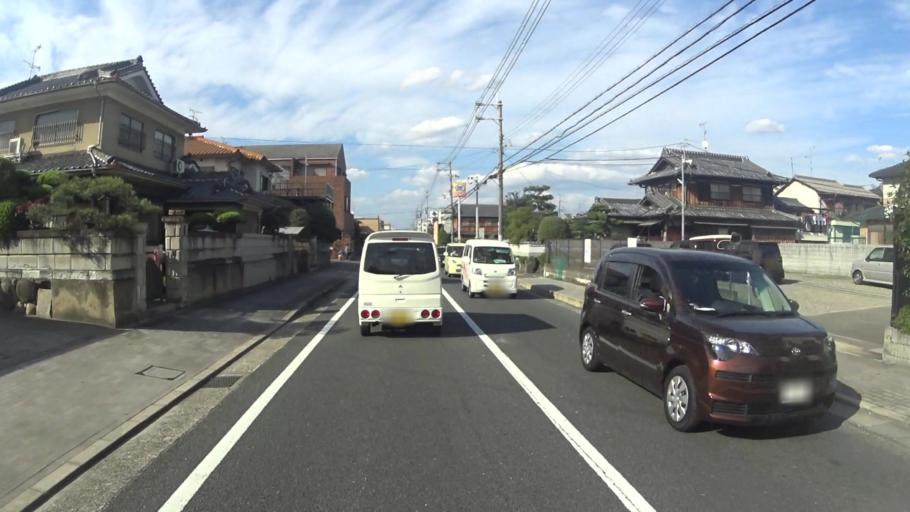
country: JP
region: Kyoto
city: Yawata
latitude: 34.8679
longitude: 135.7063
